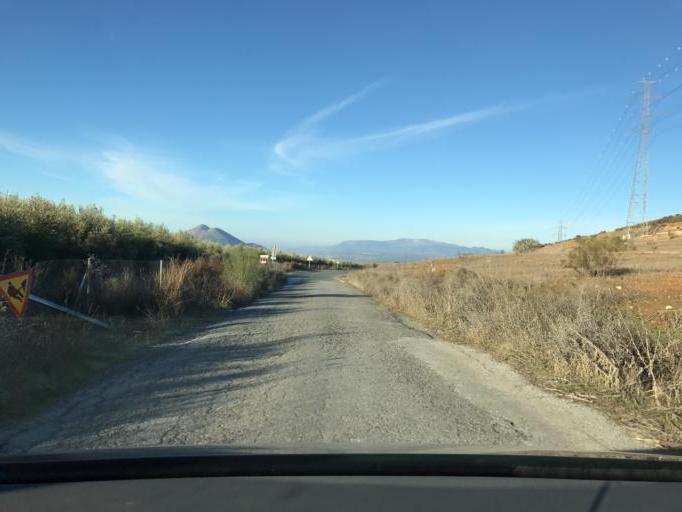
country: ES
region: Andalusia
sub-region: Provincia de Granada
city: Calicasas
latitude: 37.2610
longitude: -3.6248
